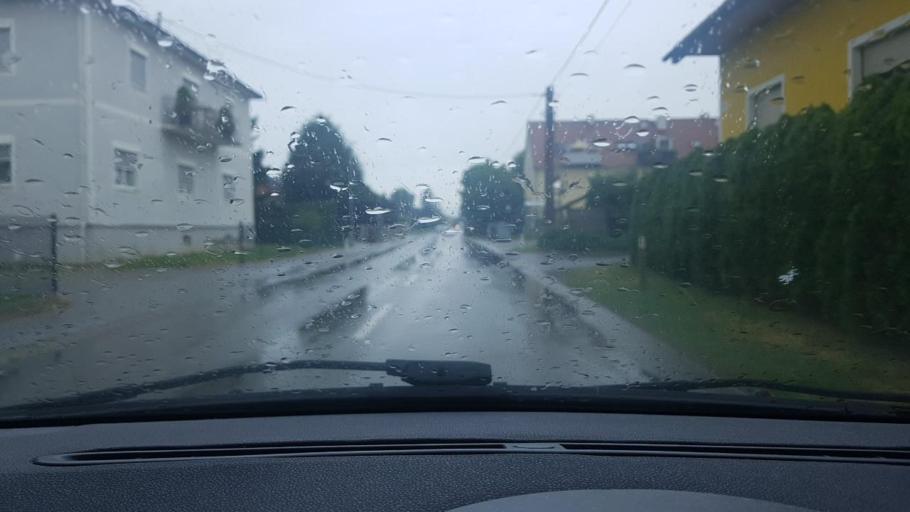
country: AT
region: Styria
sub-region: Politischer Bezirk Graz-Umgebung
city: Zettling
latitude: 46.9511
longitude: 15.4365
